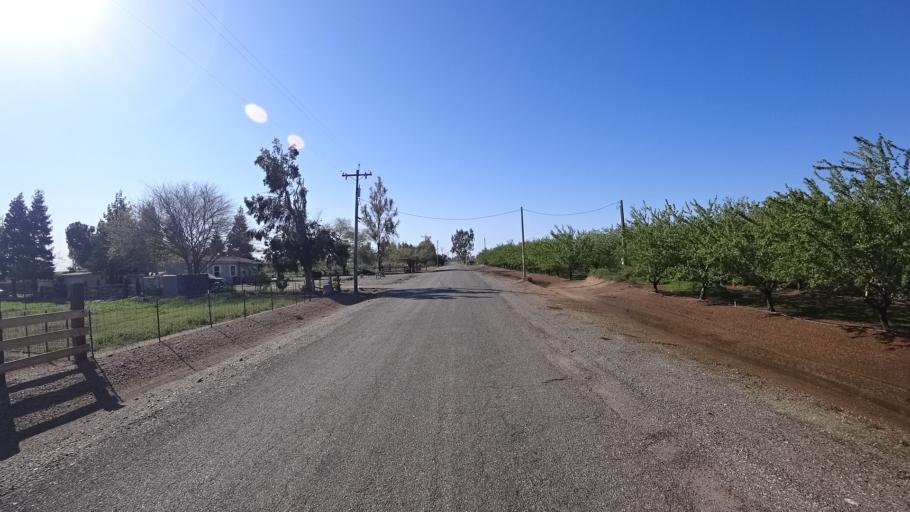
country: US
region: California
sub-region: Glenn County
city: Hamilton City
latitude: 39.7735
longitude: -122.0477
